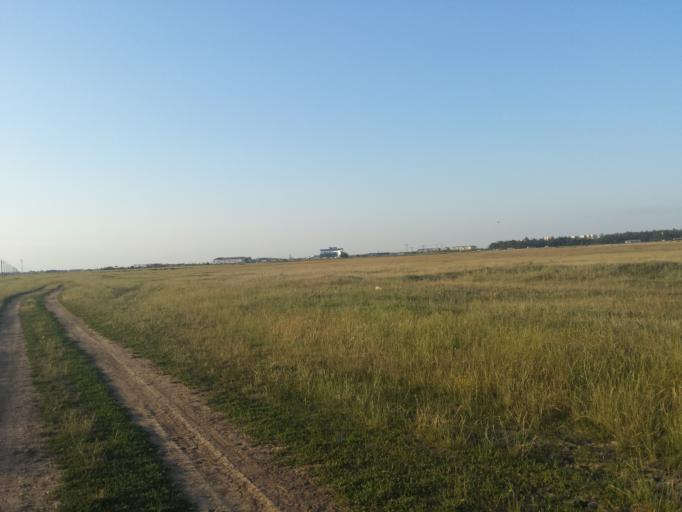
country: RO
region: Ilfov
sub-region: Comuna Tunari
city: Tunari
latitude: 44.5184
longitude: 26.1528
